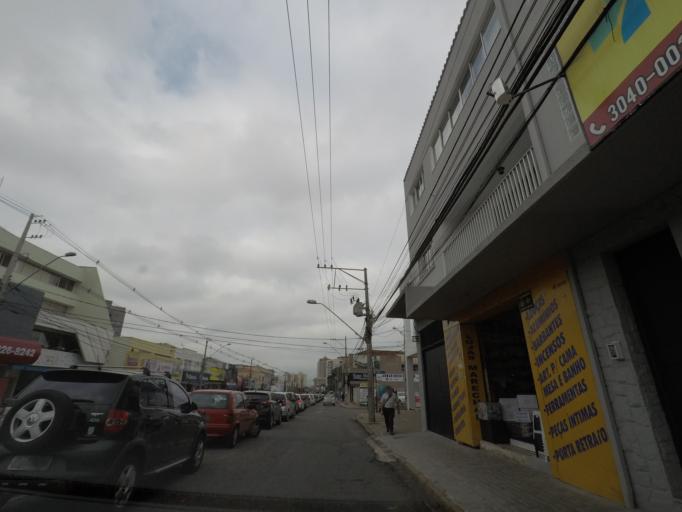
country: BR
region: Parana
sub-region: Curitiba
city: Curitiba
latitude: -25.4827
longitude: -49.2932
